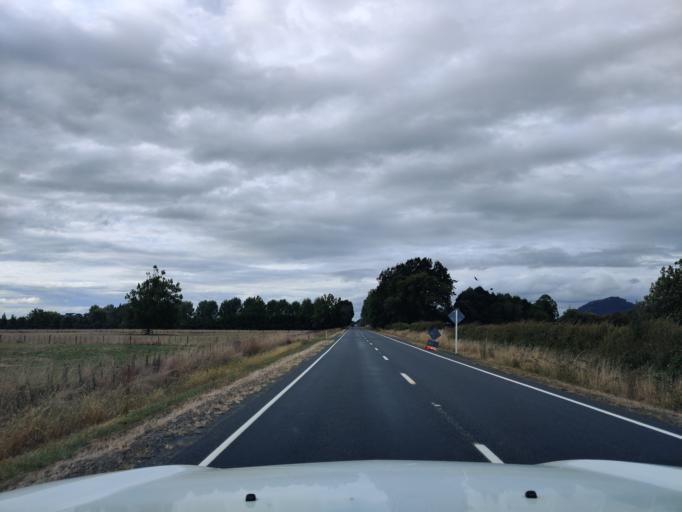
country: NZ
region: Waikato
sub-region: Waipa District
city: Cambridge
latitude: -37.8544
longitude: 175.4535
